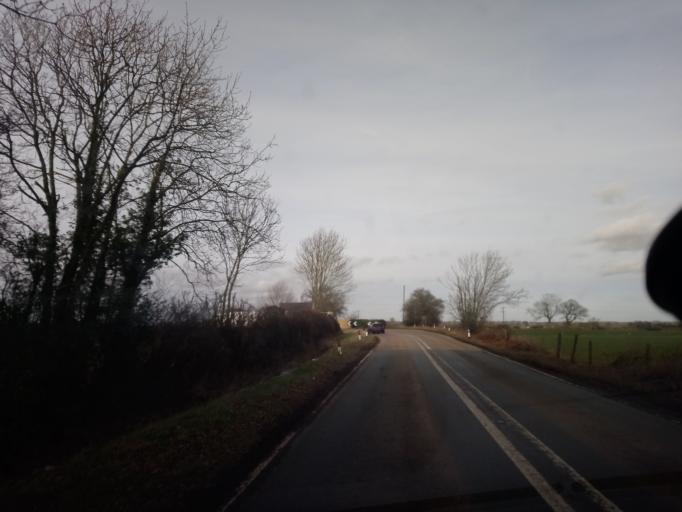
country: GB
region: England
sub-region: Shropshire
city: Prees
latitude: 52.8683
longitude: -2.6059
